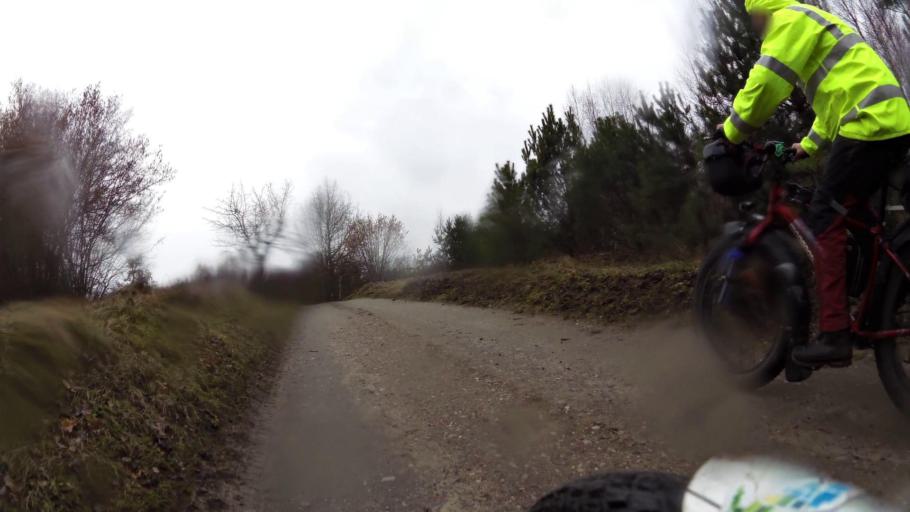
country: PL
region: Pomeranian Voivodeship
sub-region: Powiat bytowski
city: Miastko
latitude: 54.0443
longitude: 17.0477
